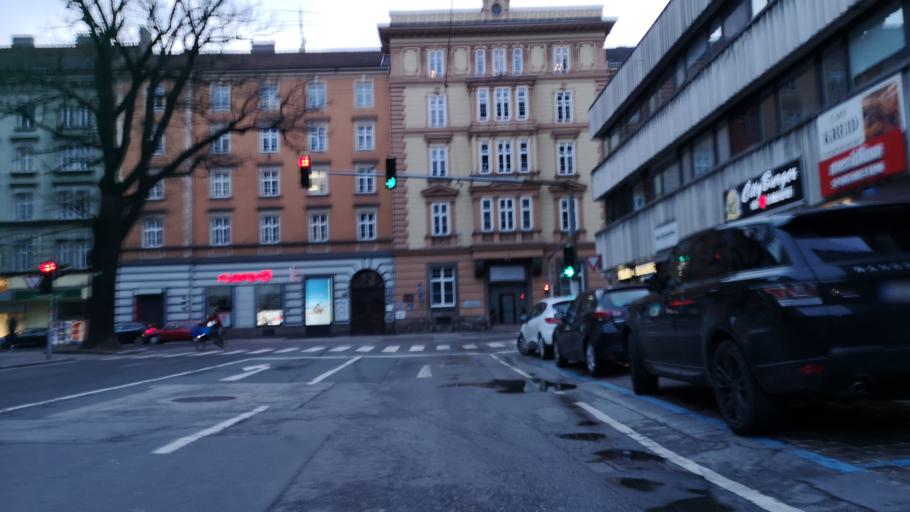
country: AT
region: Tyrol
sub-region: Innsbruck Stadt
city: Innsbruck
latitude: 47.2653
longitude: 11.3988
